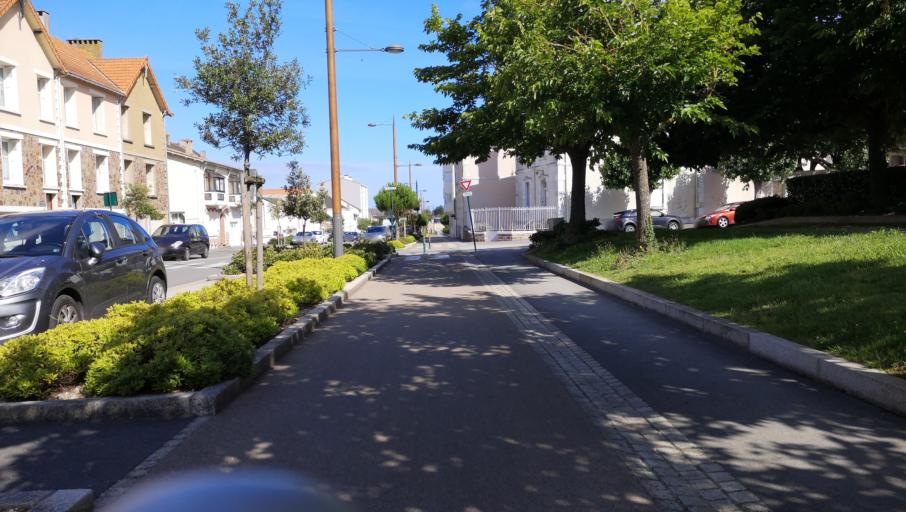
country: FR
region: Pays de la Loire
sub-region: Departement de la Vendee
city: Les Sables-d'Olonne
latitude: 46.4930
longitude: -1.7709
